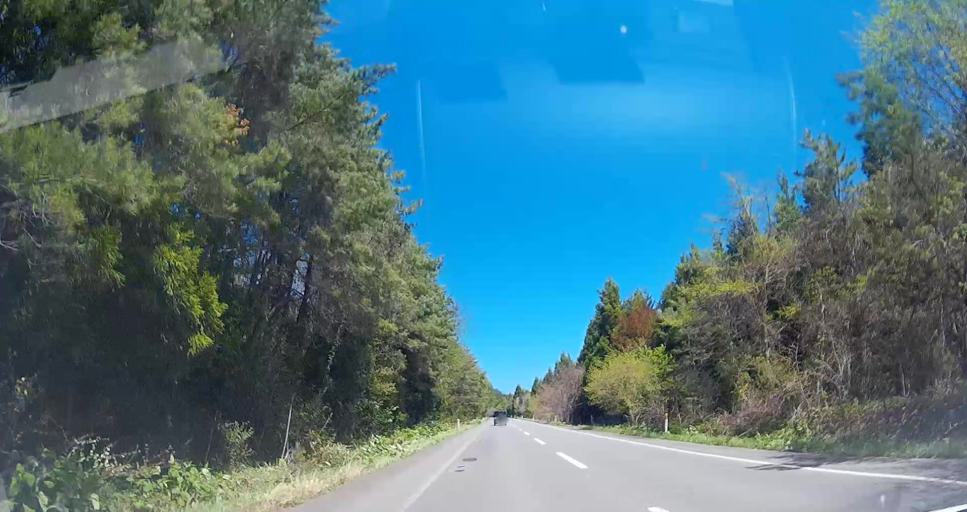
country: JP
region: Aomori
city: Mutsu
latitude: 41.3157
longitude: 141.4012
